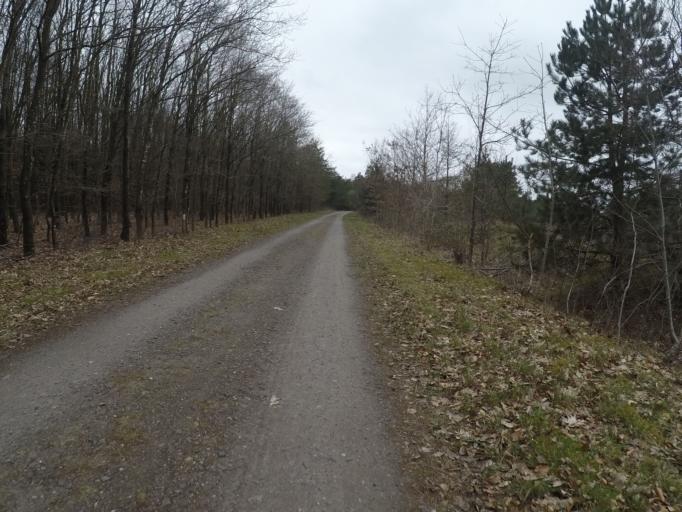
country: DE
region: Lower Saxony
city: Nordholz
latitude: 53.8079
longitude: 8.6323
